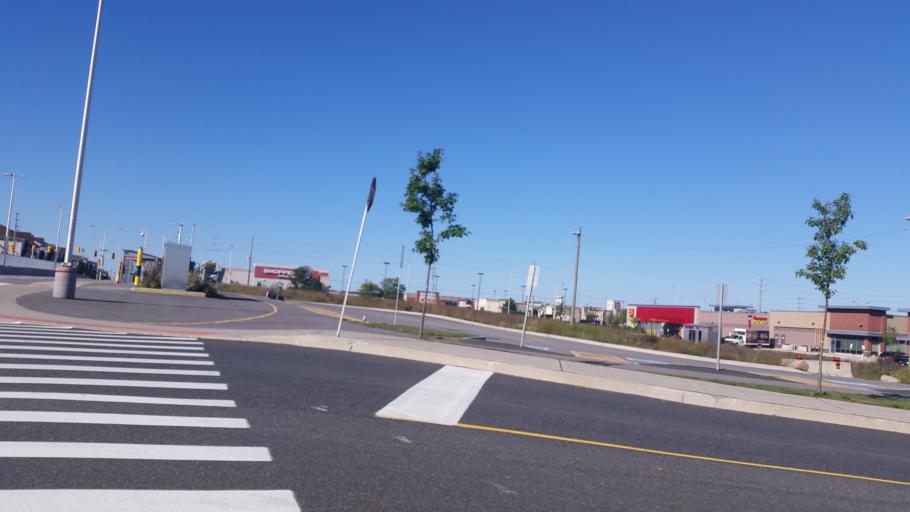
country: CA
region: Ontario
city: Bells Corners
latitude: 45.2752
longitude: -75.7157
